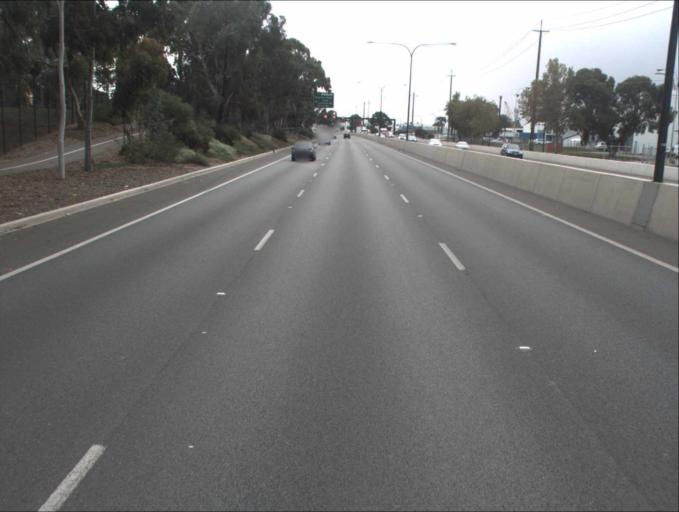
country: AU
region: South Australia
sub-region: Charles Sturt
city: Woodville
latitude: -34.8687
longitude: 138.5707
